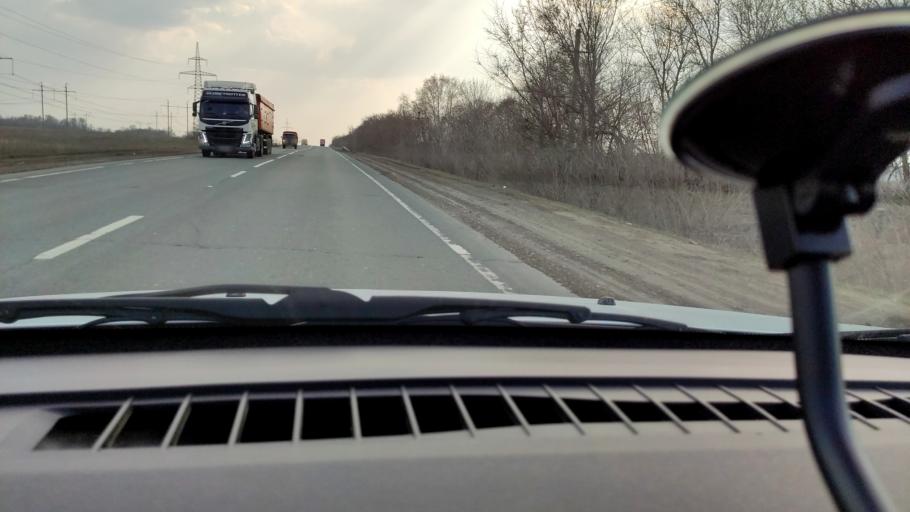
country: RU
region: Samara
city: Dubovyy Umet
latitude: 53.0790
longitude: 50.3890
